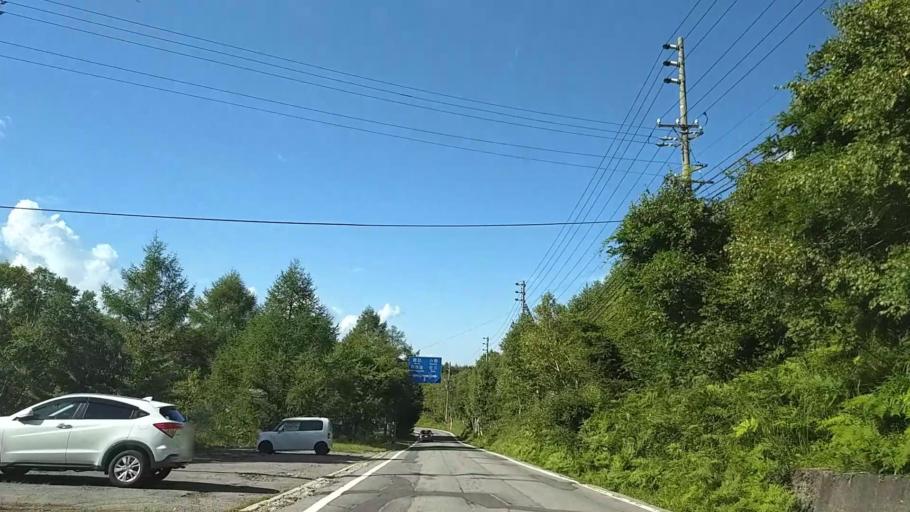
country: JP
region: Nagano
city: Chino
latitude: 36.1099
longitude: 138.2458
